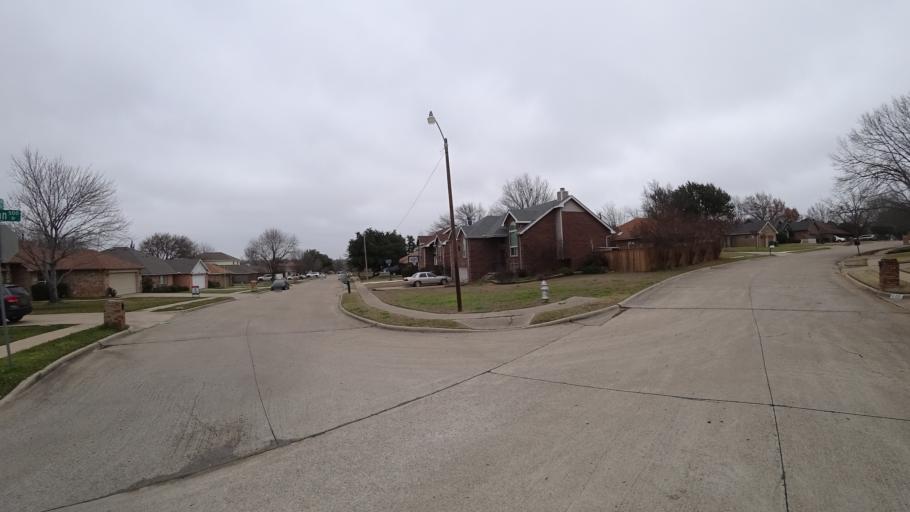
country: US
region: Texas
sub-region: Denton County
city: Lewisville
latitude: 33.0520
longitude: -97.0059
